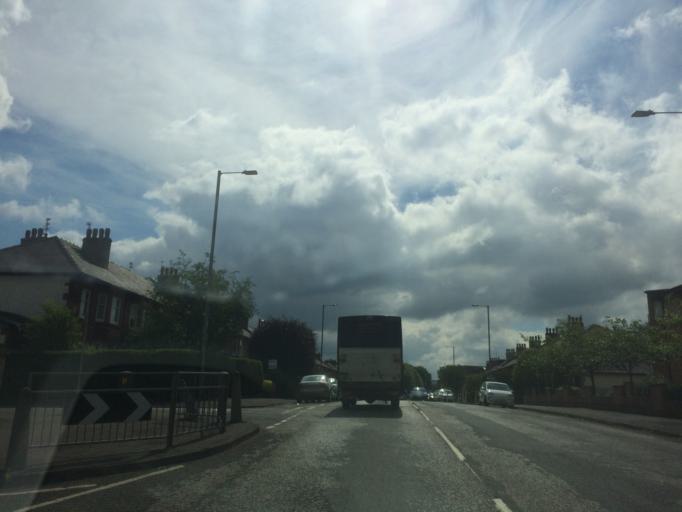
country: GB
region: Scotland
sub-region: East Renfrewshire
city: Giffnock
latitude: 55.8189
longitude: -4.2959
